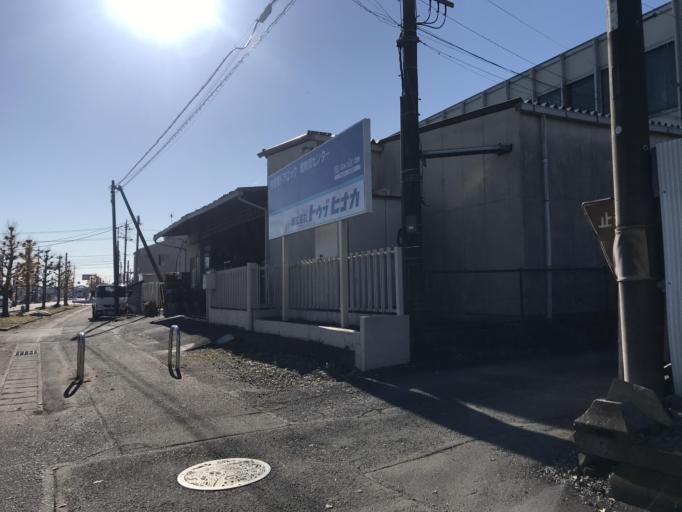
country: JP
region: Ibaraki
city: Sakai
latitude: 36.1242
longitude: 139.7993
